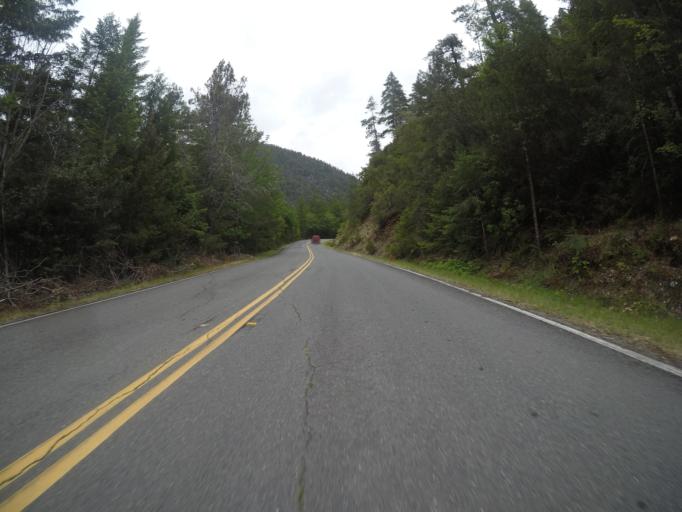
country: US
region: California
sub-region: Del Norte County
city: Bertsch-Oceanview
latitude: 41.7258
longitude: -123.9646
